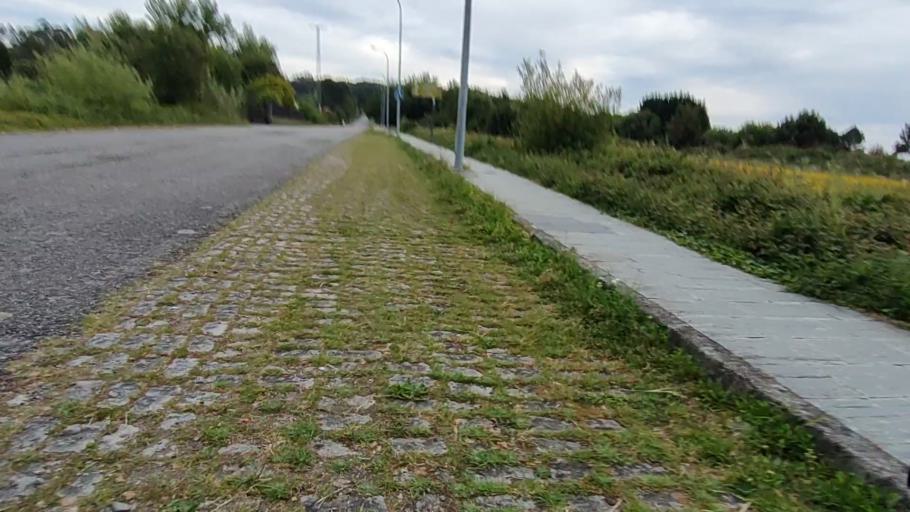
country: ES
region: Galicia
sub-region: Provincia da Coruna
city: Boiro
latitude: 42.6119
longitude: -8.8670
